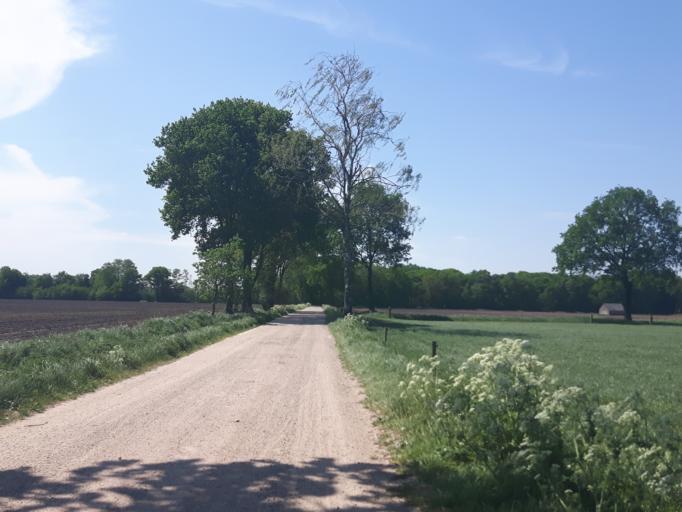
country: NL
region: Overijssel
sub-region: Gemeente Enschede
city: Enschede
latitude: 52.1586
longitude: 6.8850
